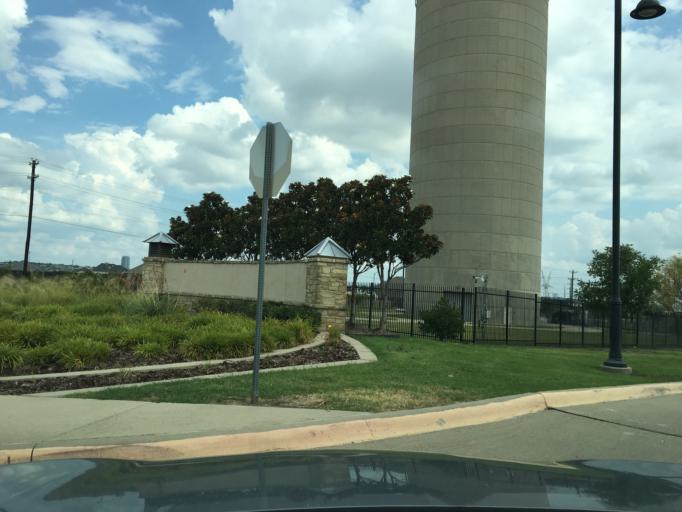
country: US
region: Texas
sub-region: Collin County
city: Frisco
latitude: 33.1293
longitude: -96.8615
